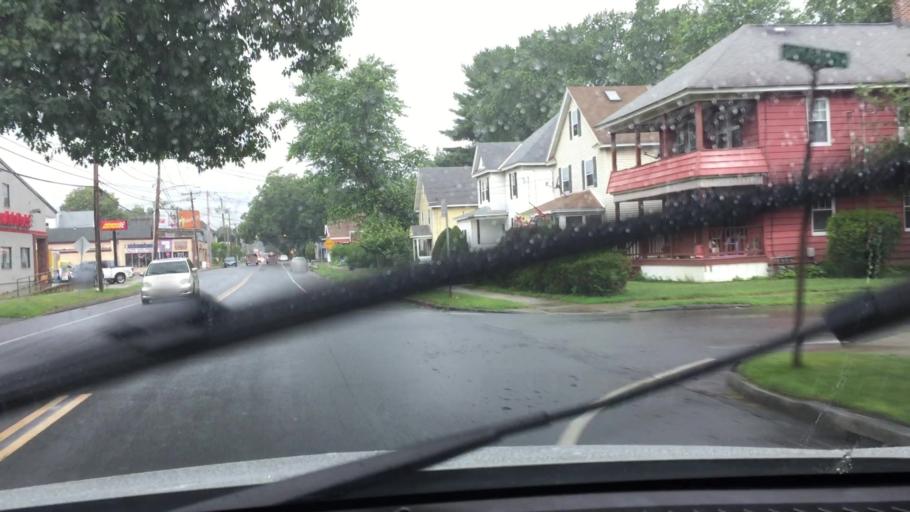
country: US
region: Massachusetts
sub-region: Berkshire County
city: Pittsfield
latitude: 42.4432
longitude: -73.2337
